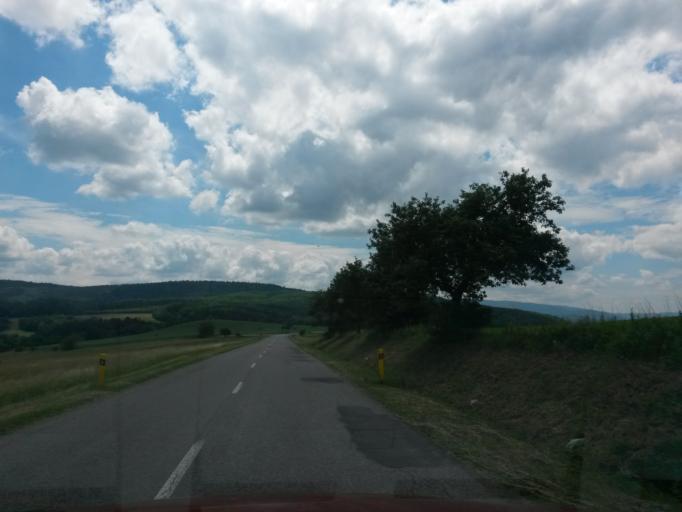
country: SK
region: Kosicky
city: Gelnica
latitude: 48.9306
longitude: 21.0460
